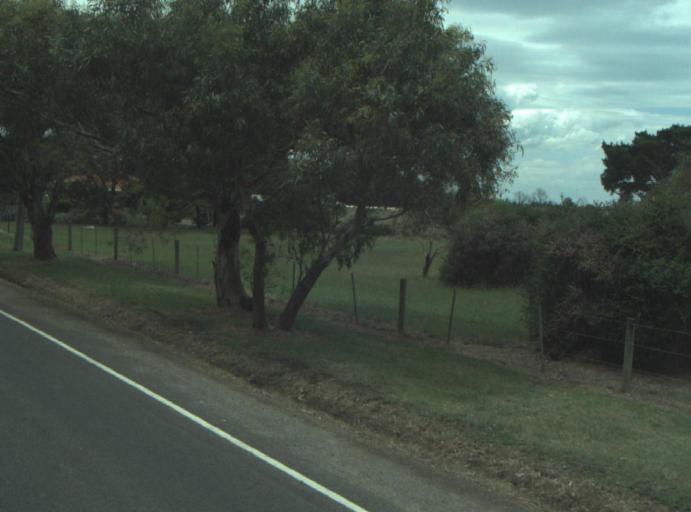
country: AU
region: Victoria
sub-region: Greater Geelong
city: Leopold
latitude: -38.1833
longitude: 144.4562
